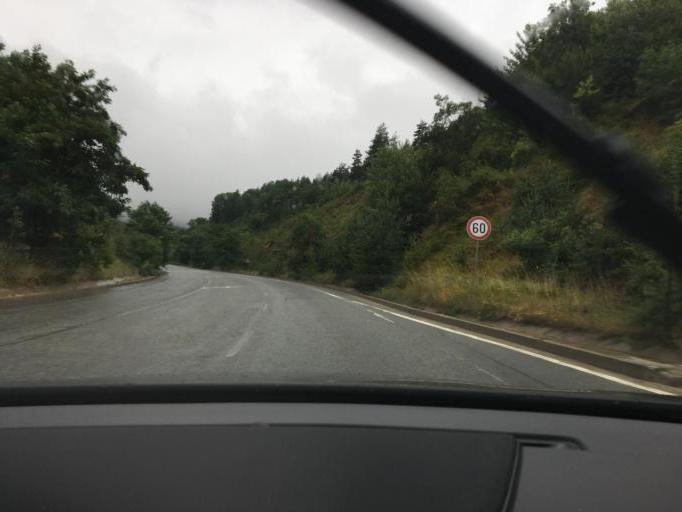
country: BG
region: Kyustendil
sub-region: Obshtina Kyustendil
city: Kyustendil
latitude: 42.2663
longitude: 22.5787
